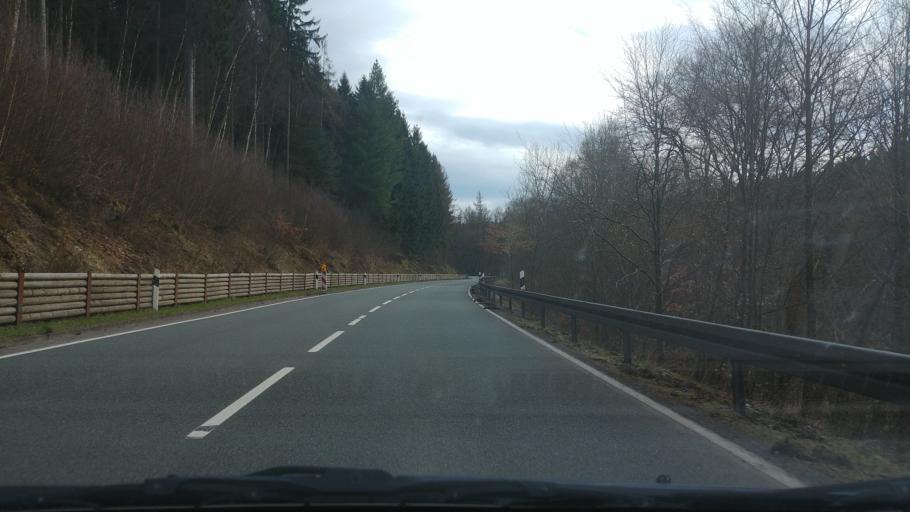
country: DE
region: Lower Saxony
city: Bevern
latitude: 51.8114
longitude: 9.4945
